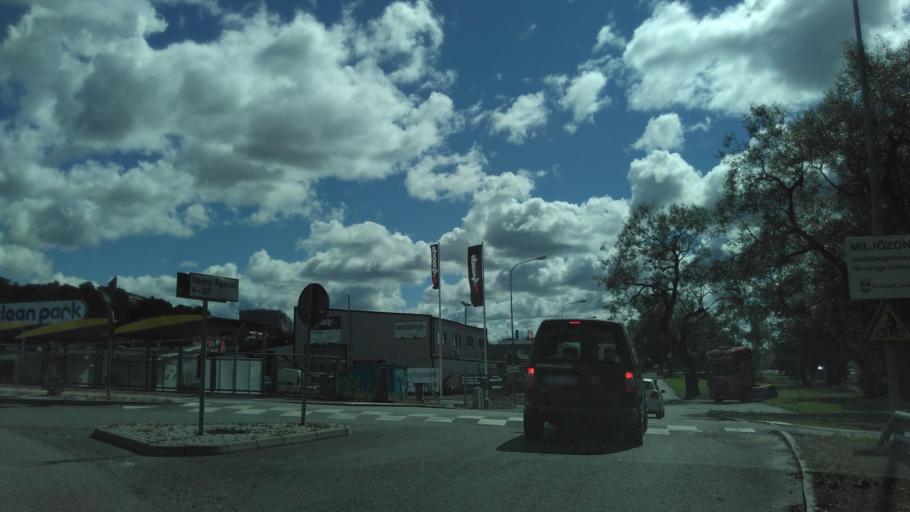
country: SE
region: Vaestra Goetaland
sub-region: Molndal
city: Moelndal
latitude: 57.6648
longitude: 12.0132
